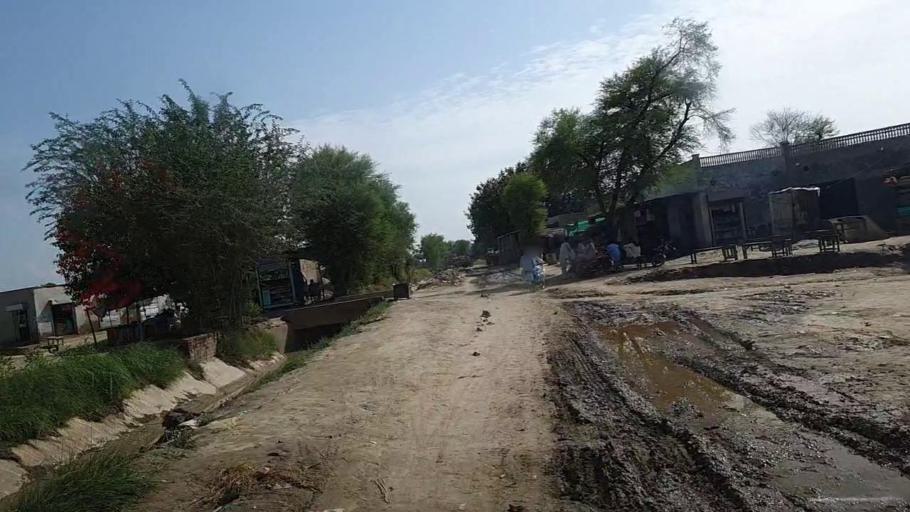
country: PK
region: Sindh
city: Bhiria
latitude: 26.8783
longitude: 68.2301
